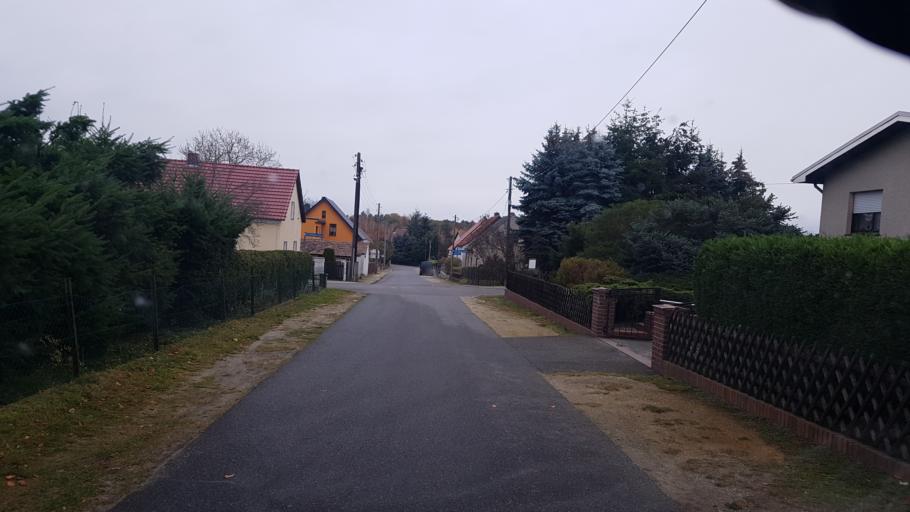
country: DE
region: Brandenburg
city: Crinitz
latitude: 51.7375
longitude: 13.7689
